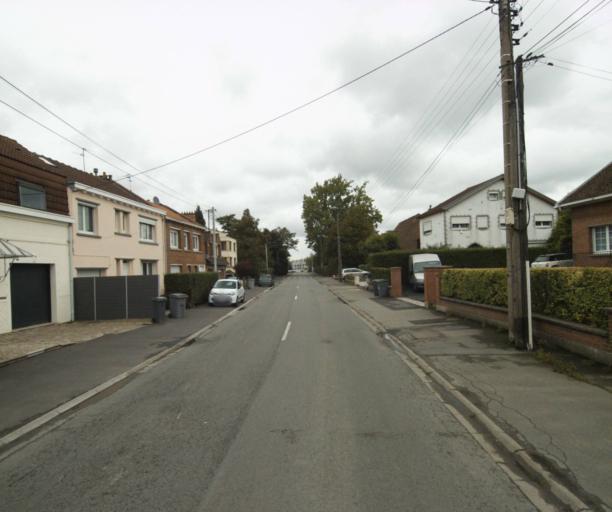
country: FR
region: Nord-Pas-de-Calais
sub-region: Departement du Nord
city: Vendeville
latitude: 50.5862
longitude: 3.0824
